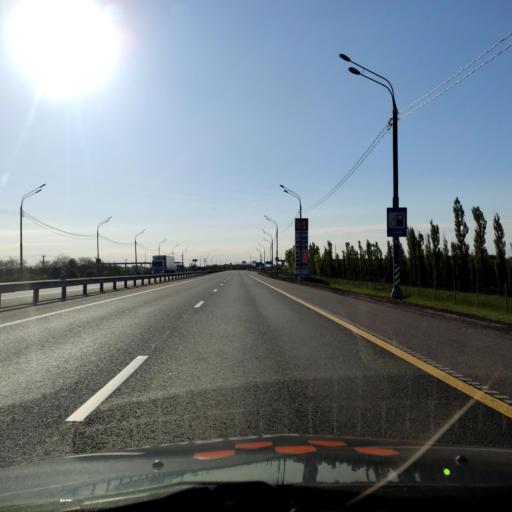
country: RU
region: Lipetsk
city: Khlevnoye
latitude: 52.2198
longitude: 39.1277
